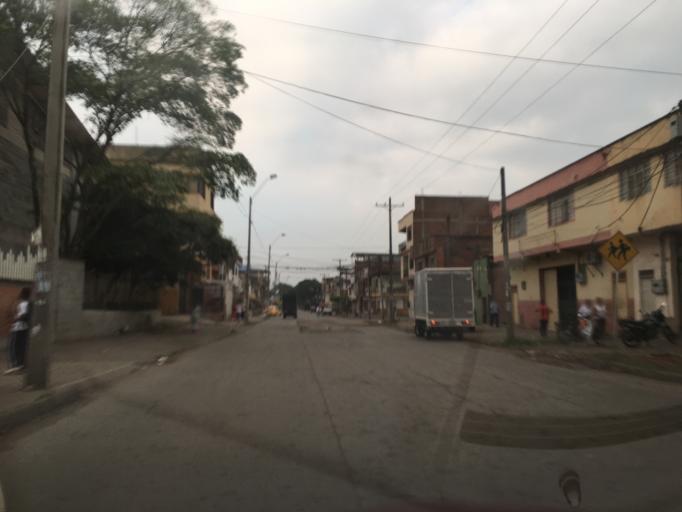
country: CO
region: Valle del Cauca
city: Cali
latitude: 3.4242
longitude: -76.5214
